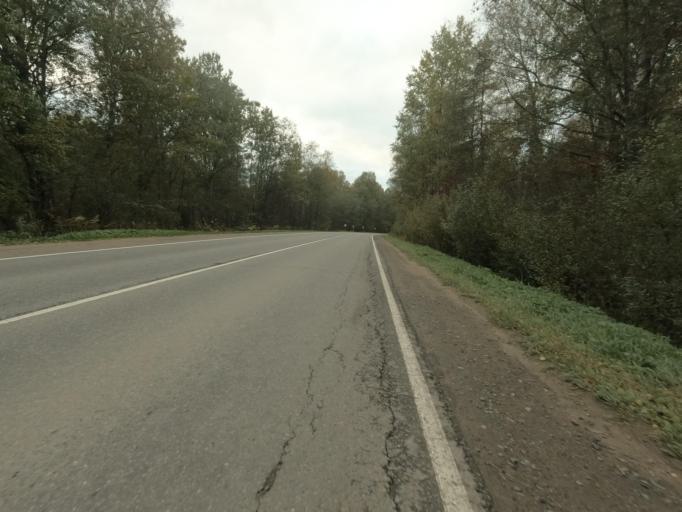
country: RU
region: Leningrad
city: Pavlovo
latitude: 59.7966
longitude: 30.9472
